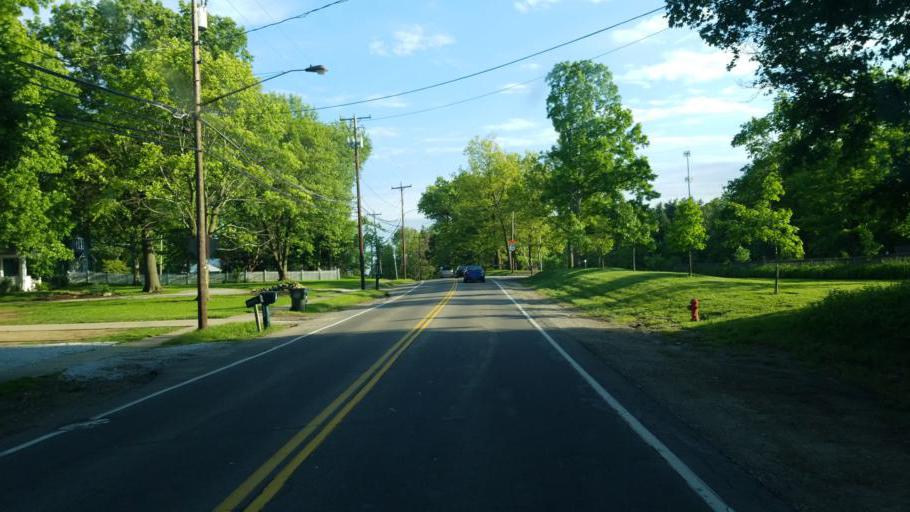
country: US
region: Ohio
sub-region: Summit County
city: Stow
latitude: 41.1560
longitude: -81.4402
